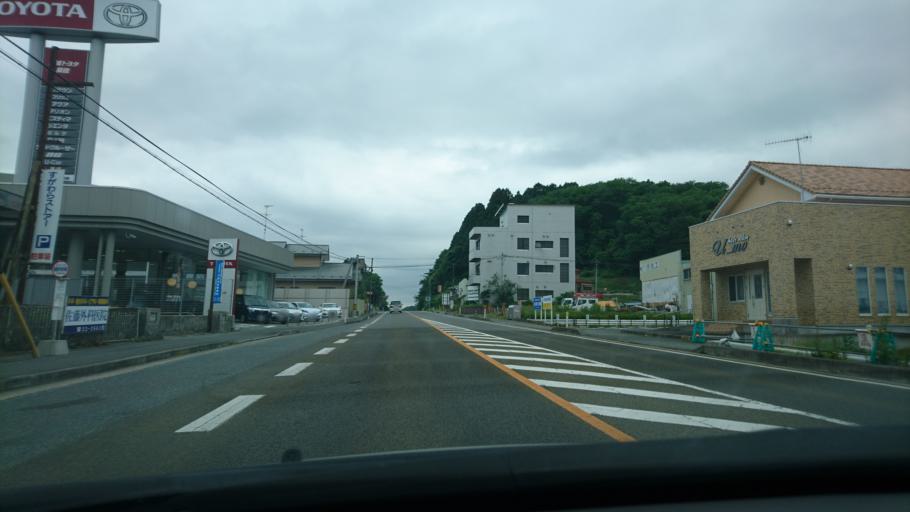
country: JP
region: Miyagi
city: Furukawa
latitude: 38.7286
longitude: 141.0220
